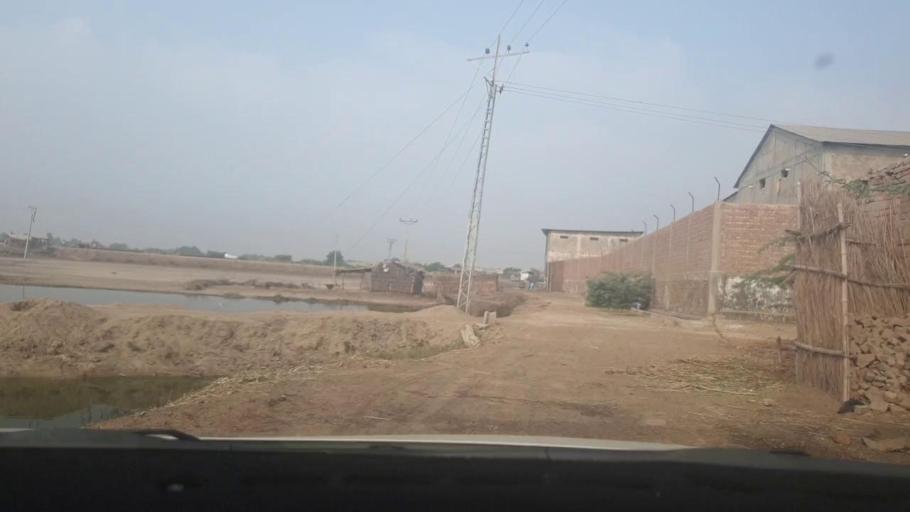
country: PK
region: Sindh
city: Tando Muhammad Khan
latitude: 25.1096
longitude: 68.5372
